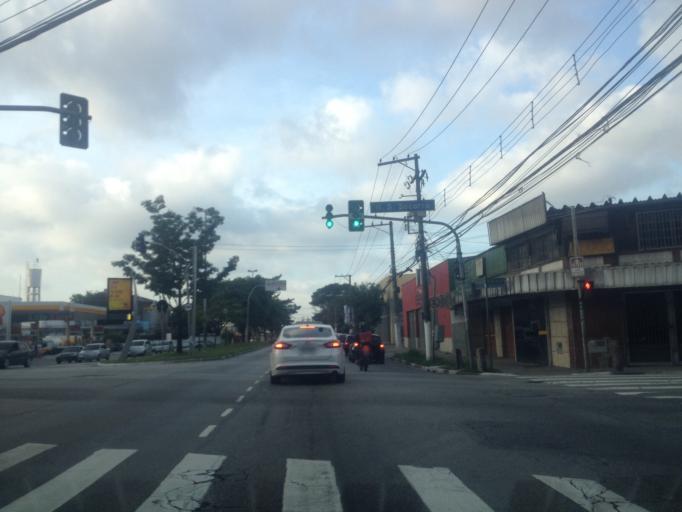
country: BR
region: Sao Paulo
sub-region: Diadema
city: Diadema
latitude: -23.6717
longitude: -46.7121
